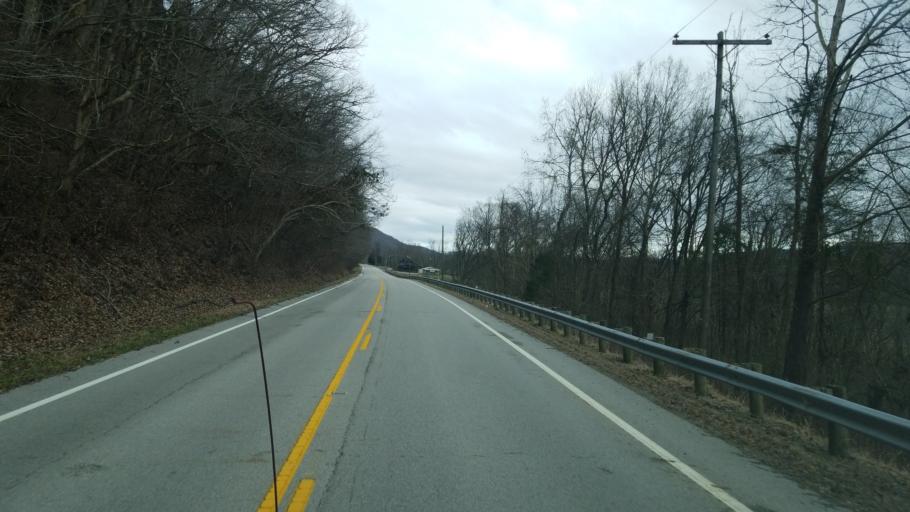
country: US
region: Kentucky
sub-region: Lewis County
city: Vanceburg
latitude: 38.6627
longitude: -83.3646
